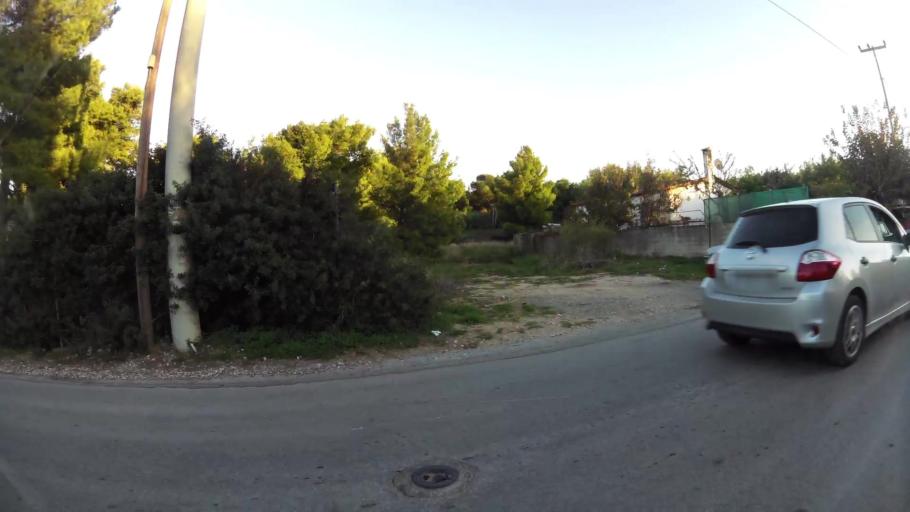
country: GR
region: Attica
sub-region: Nomarchia Anatolikis Attikis
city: Rafina
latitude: 38.0081
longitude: 24.0094
